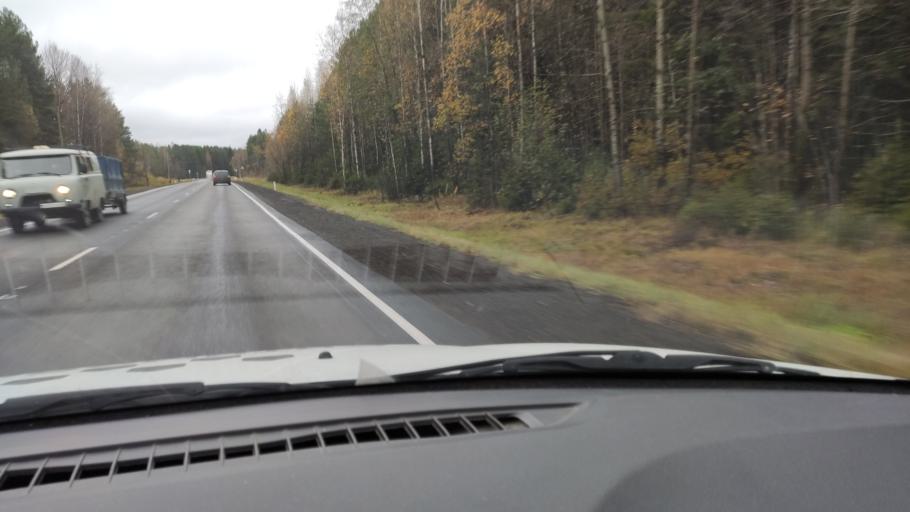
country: RU
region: Kirov
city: Belaya Kholunitsa
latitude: 58.8756
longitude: 50.8628
